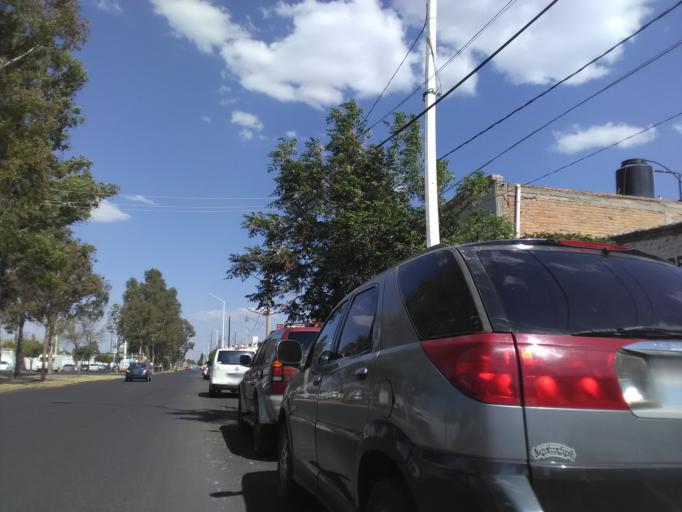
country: MX
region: Durango
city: Victoria de Durango
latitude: 24.0269
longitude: -104.6360
